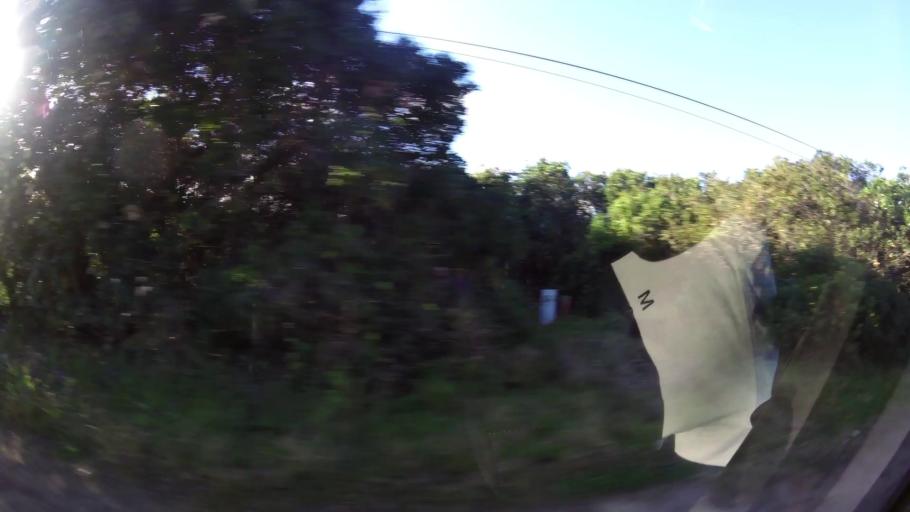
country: ZA
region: Western Cape
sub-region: Eden District Municipality
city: George
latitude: -34.0013
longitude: 22.6331
